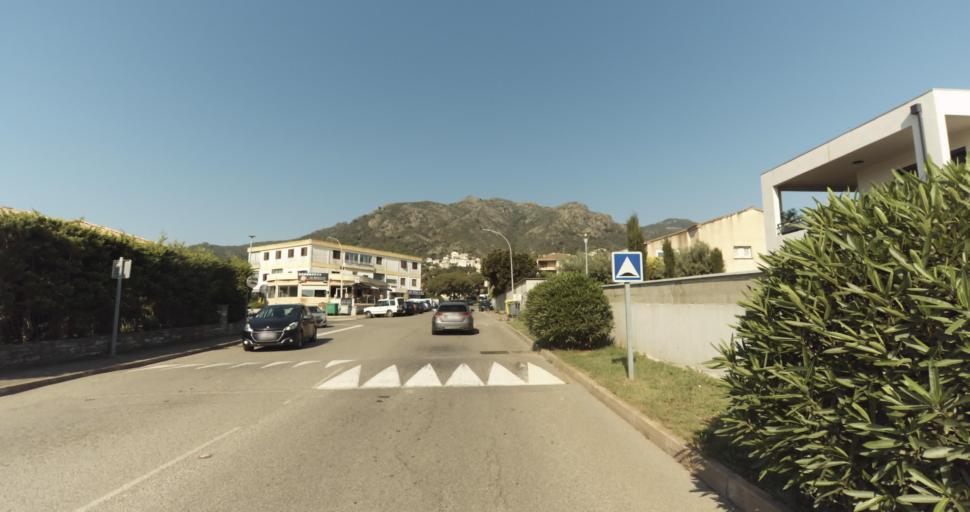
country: FR
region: Corsica
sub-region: Departement de la Haute-Corse
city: Biguglia
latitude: 42.6286
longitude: 9.4317
